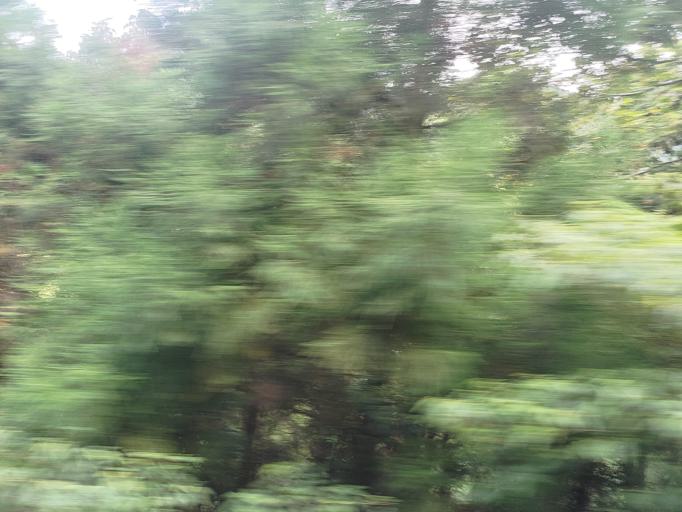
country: TW
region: Taiwan
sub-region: Hsinchu
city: Hsinchu
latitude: 24.6277
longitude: 121.0790
